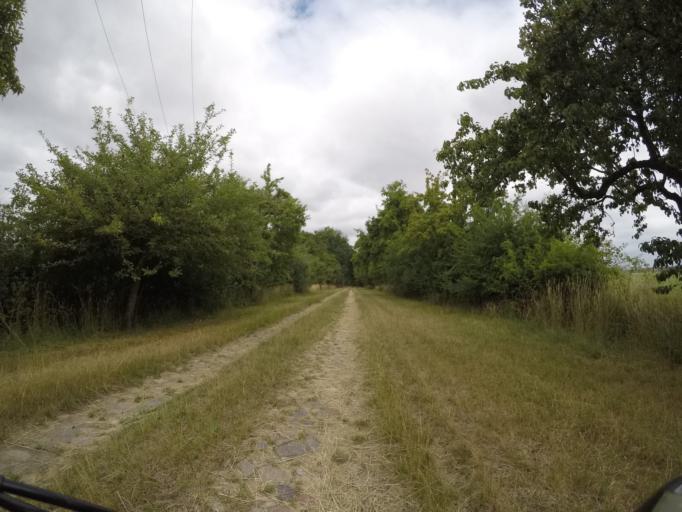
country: DE
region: Lower Saxony
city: Hitzacker
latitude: 53.1683
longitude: 11.0451
